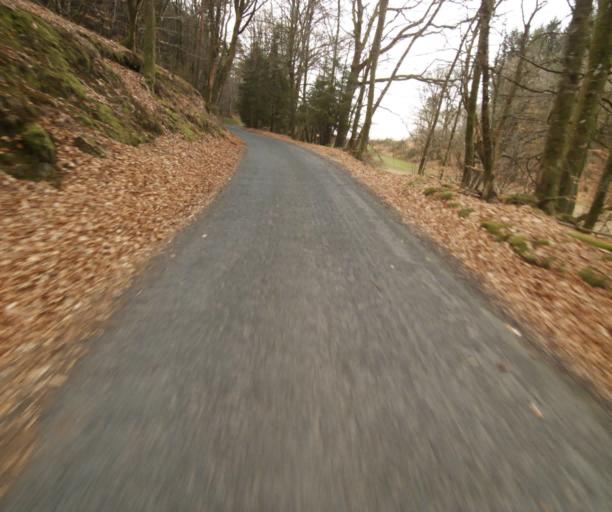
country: FR
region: Limousin
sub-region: Departement de la Correze
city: Treignac
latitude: 45.4483
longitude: 1.8192
